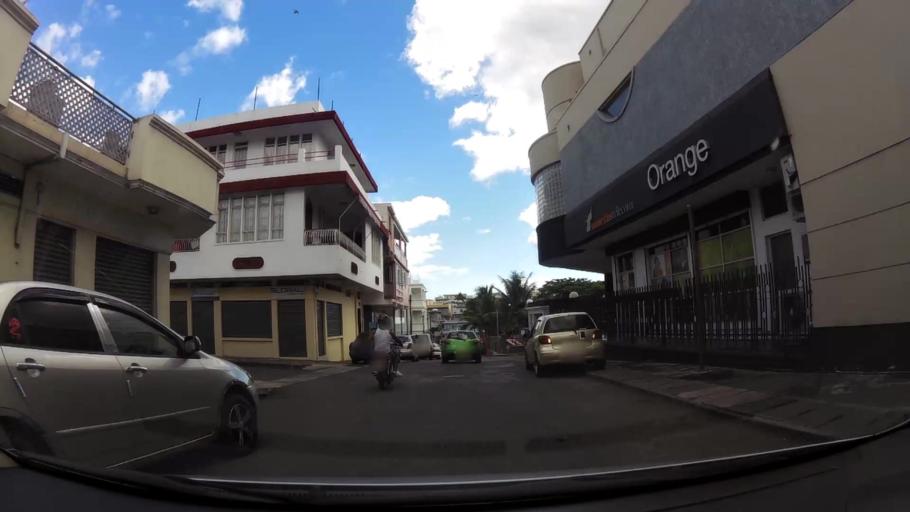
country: MU
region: Port Louis
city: Port Louis
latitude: -20.1563
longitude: 57.5084
